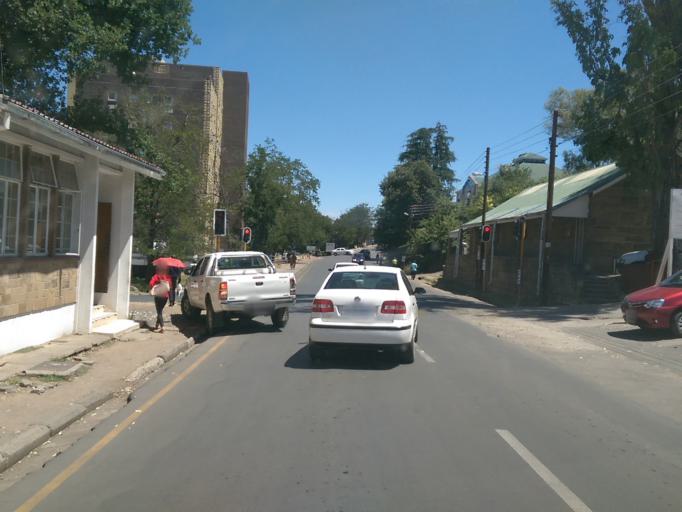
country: LS
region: Maseru
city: Maseru
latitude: -29.3129
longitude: 27.4814
